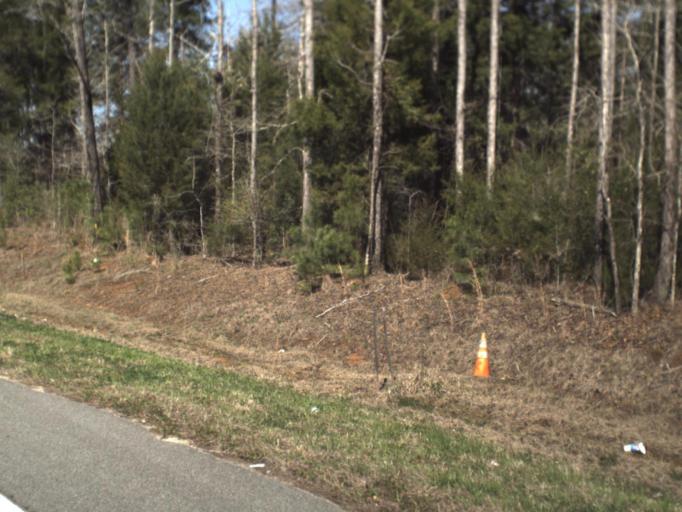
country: US
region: Florida
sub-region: Jackson County
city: Marianna
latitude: 30.7991
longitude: -85.2743
